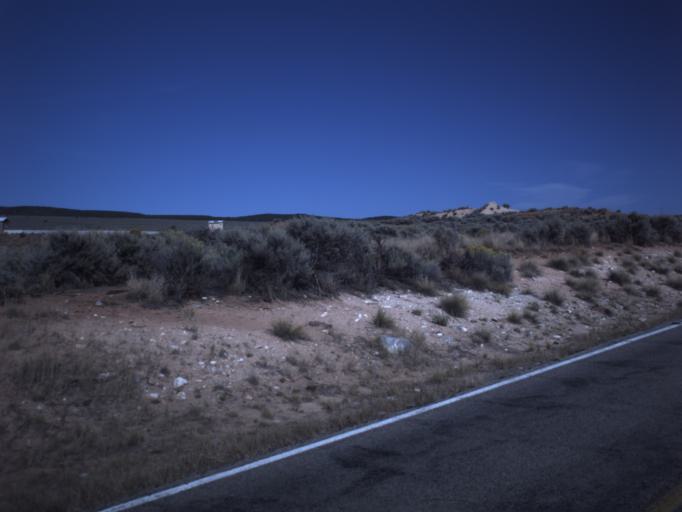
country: US
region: Utah
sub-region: Grand County
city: Moab
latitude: 38.3152
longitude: -109.3080
